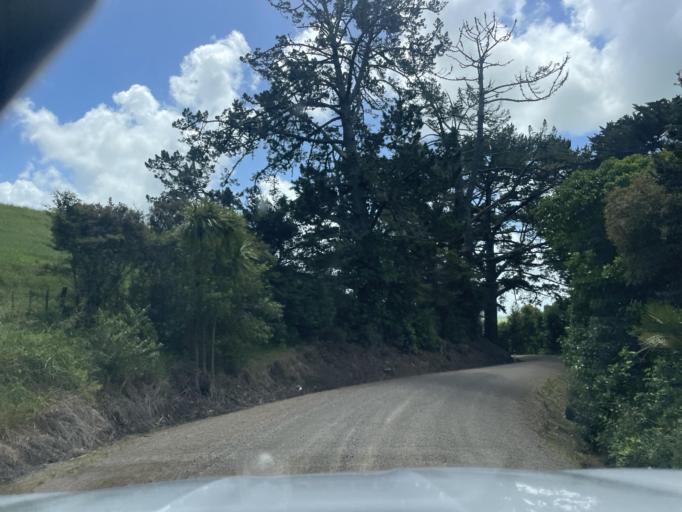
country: NZ
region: Auckland
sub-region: Auckland
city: Wellsford
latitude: -36.1842
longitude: 174.3206
